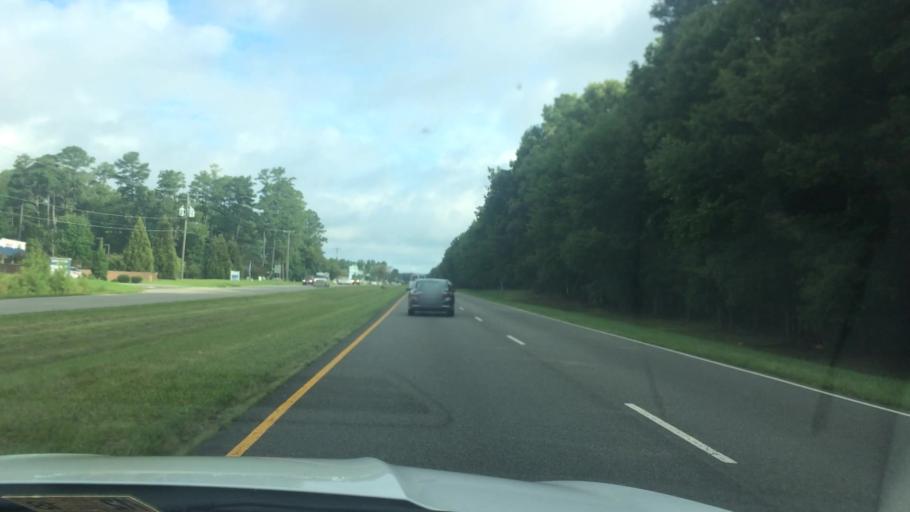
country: US
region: Virginia
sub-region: Gloucester County
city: Gloucester Courthouse
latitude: 37.3357
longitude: -76.5158
